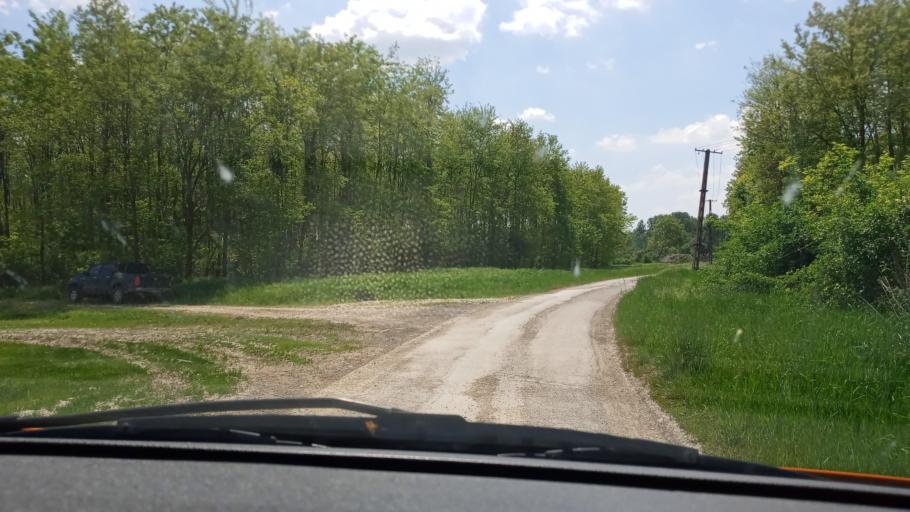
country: HU
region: Baranya
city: Siklos
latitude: 45.7698
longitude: 18.2873
